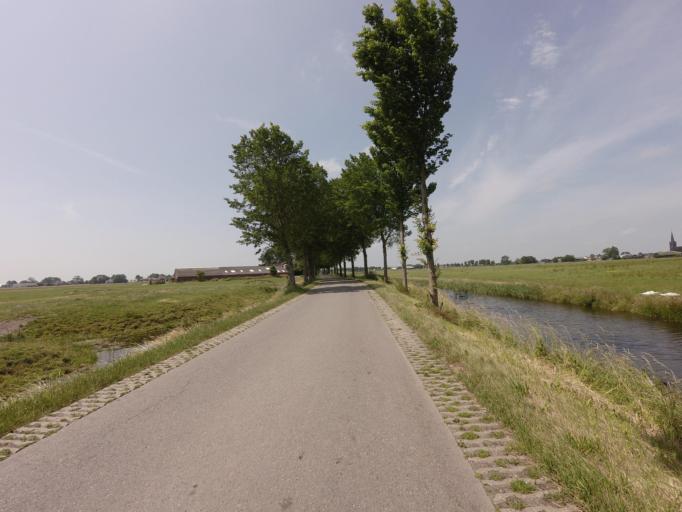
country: NL
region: North Holland
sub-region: Gemeente Opmeer
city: Opmeer
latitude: 52.6941
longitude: 4.9508
